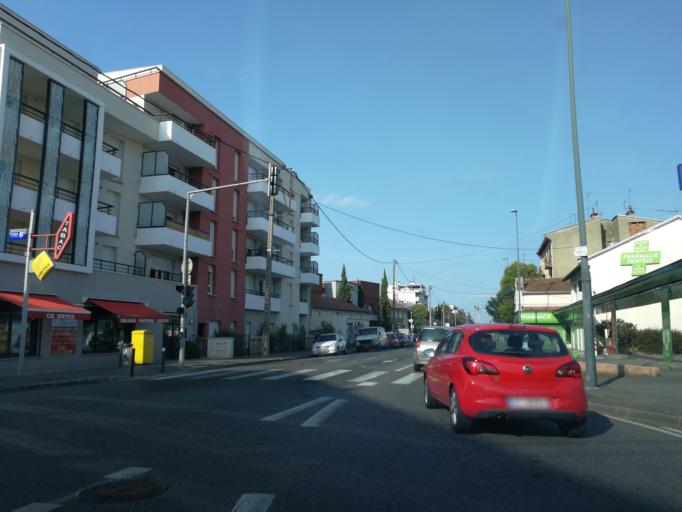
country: FR
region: Midi-Pyrenees
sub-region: Departement de la Haute-Garonne
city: Toulouse
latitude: 43.6226
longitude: 1.4256
